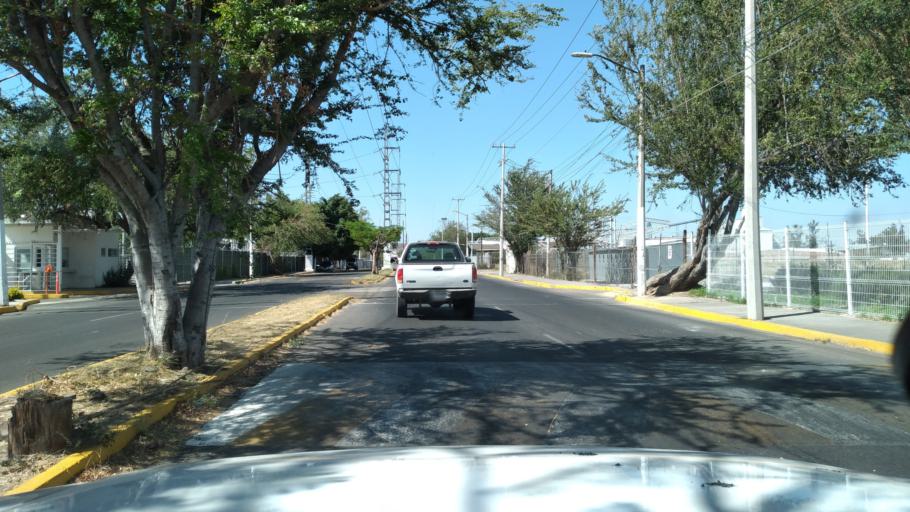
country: MX
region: Jalisco
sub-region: Zapopan
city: Zapopan
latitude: 20.7333
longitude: -103.3764
